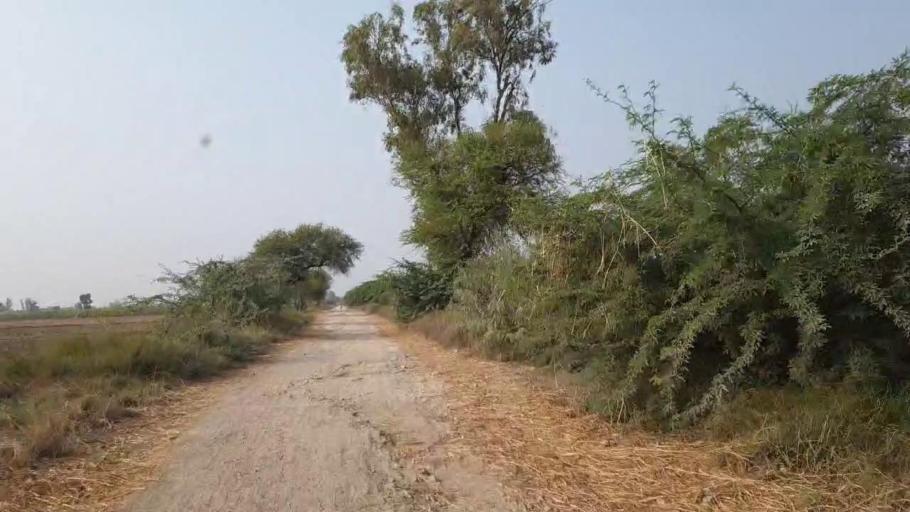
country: PK
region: Sindh
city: Tando Muhammad Khan
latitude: 25.0775
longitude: 68.5905
